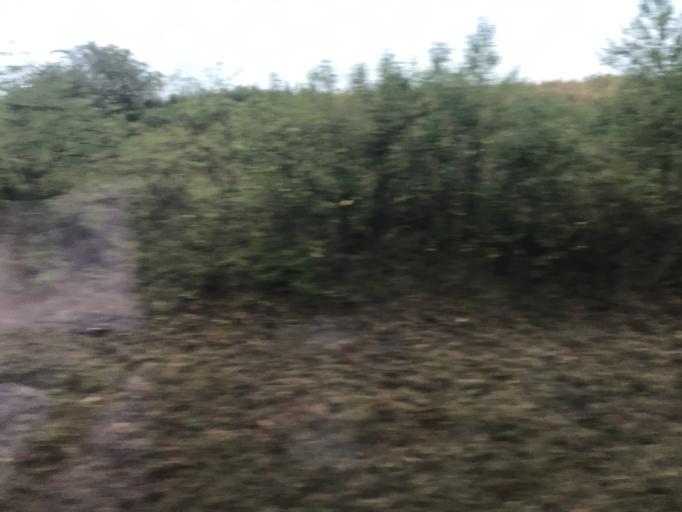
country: DE
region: Bavaria
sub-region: Regierungsbezirk Unterfranken
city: Bergtheim
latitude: 49.9134
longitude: 10.0850
